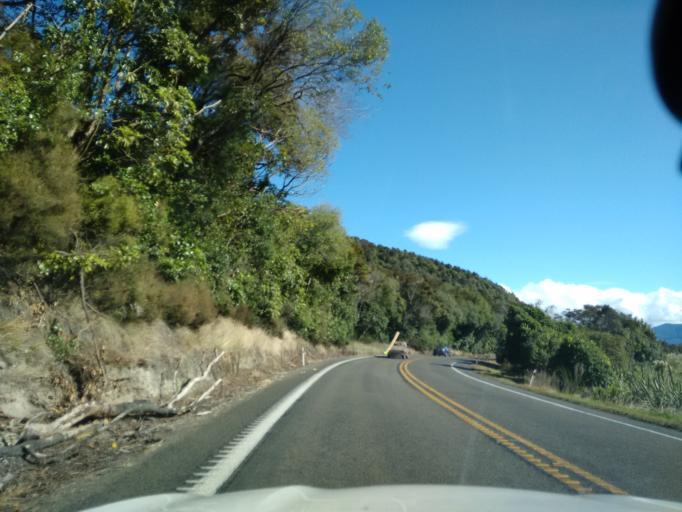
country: NZ
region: Waikato
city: Turangi
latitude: -38.9408
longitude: 175.8580
